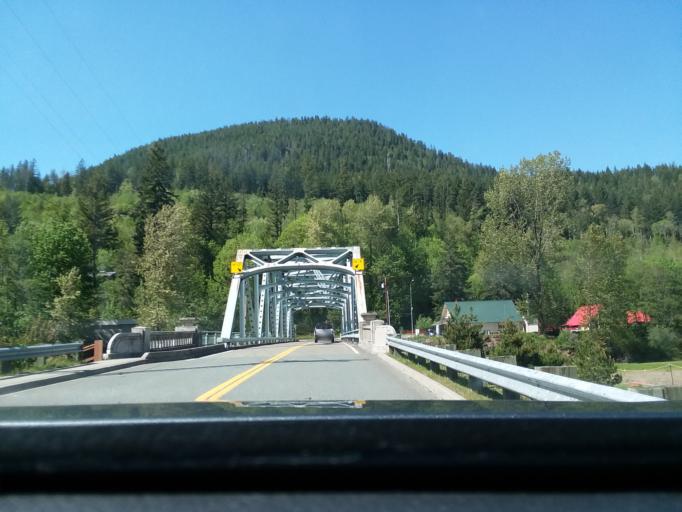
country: US
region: Washington
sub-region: Snohomish County
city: Gold Bar
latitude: 47.7101
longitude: -121.3608
